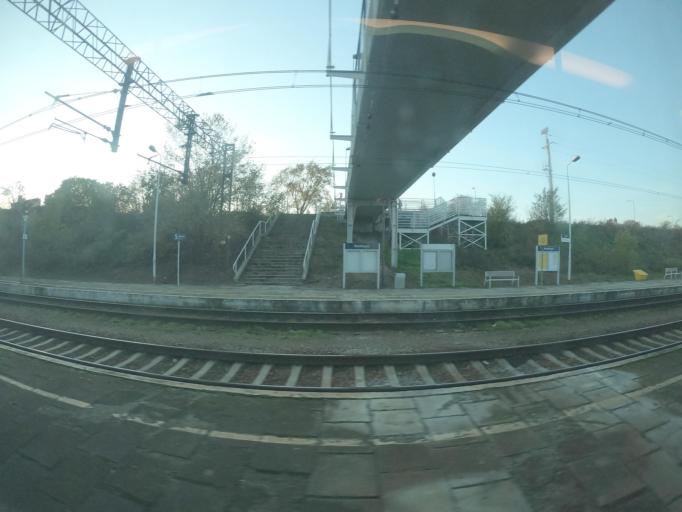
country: PL
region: Lubusz
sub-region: Powiat gorzowski
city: Kostrzyn nad Odra
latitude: 52.5916
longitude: 14.6472
